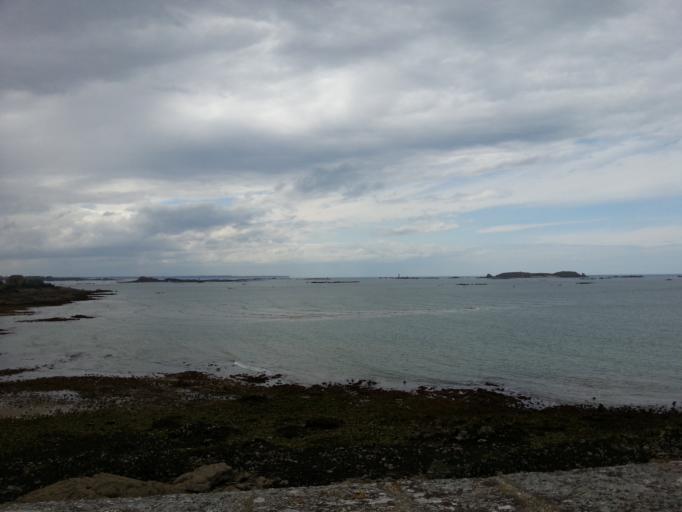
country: FR
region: Brittany
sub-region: Departement d'Ille-et-Vilaine
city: Saint-Malo
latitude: 48.6551
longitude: -2.0235
